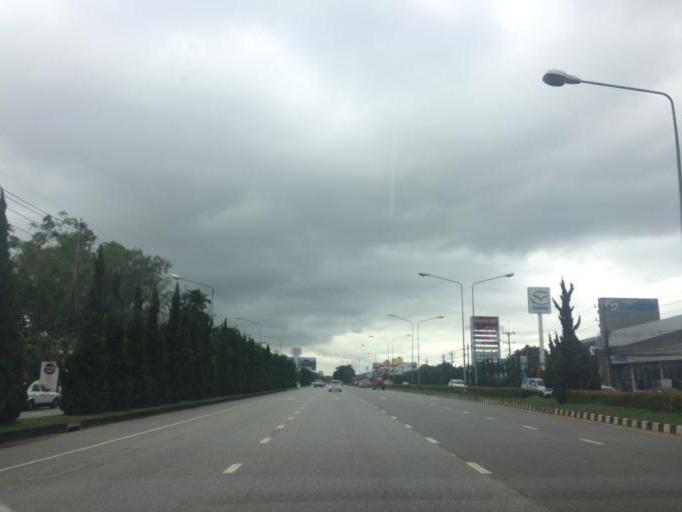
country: TH
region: Chiang Rai
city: Chiang Rai
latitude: 19.8900
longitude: 99.8365
